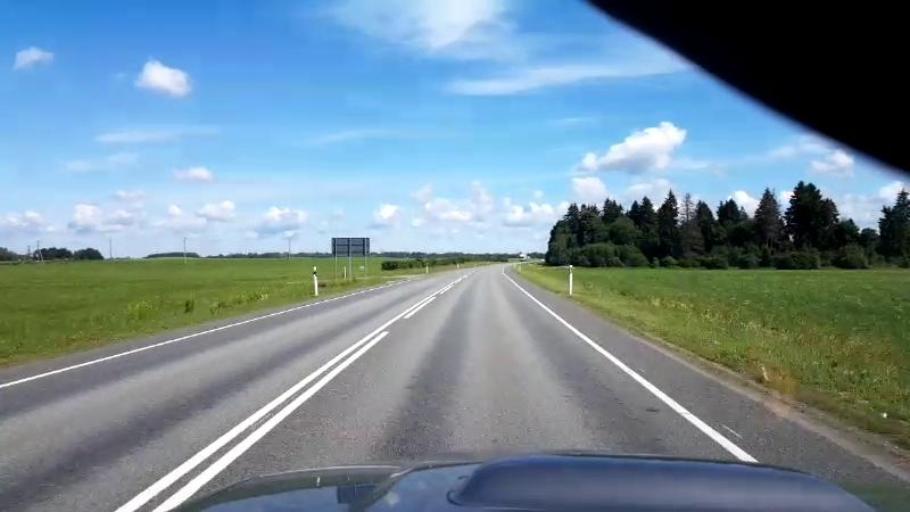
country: EE
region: Jaervamaa
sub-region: Jaerva-Jaani vald
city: Jarva-Jaani
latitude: 59.1732
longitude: 25.7578
